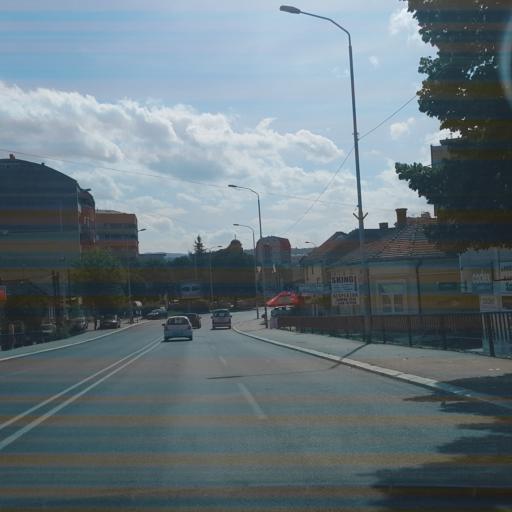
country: RS
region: Central Serbia
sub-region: Nisavski Okrug
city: Nis
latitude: 43.3256
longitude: 21.9029
